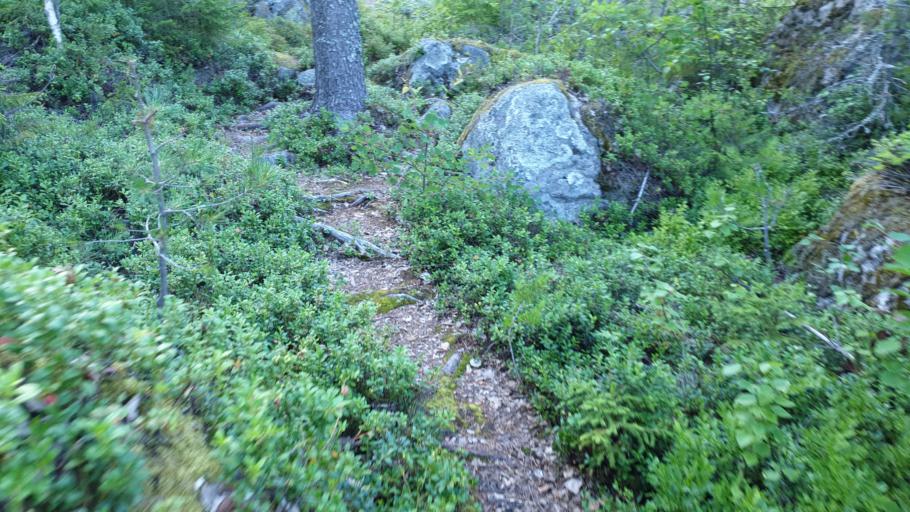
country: SE
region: Gaevleborg
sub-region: Soderhamns Kommun
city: Marielund
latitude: 61.4229
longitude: 17.1539
